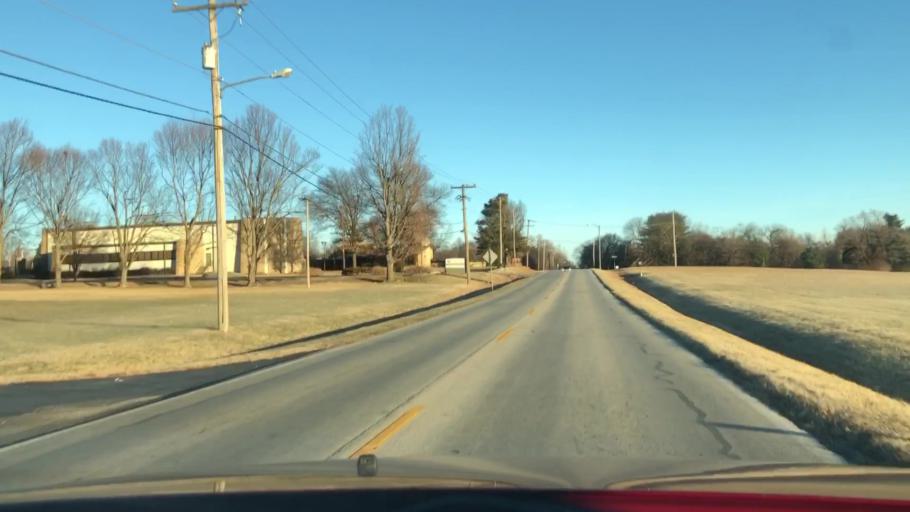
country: US
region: Missouri
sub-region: Greene County
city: Springfield
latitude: 37.1678
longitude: -93.2467
